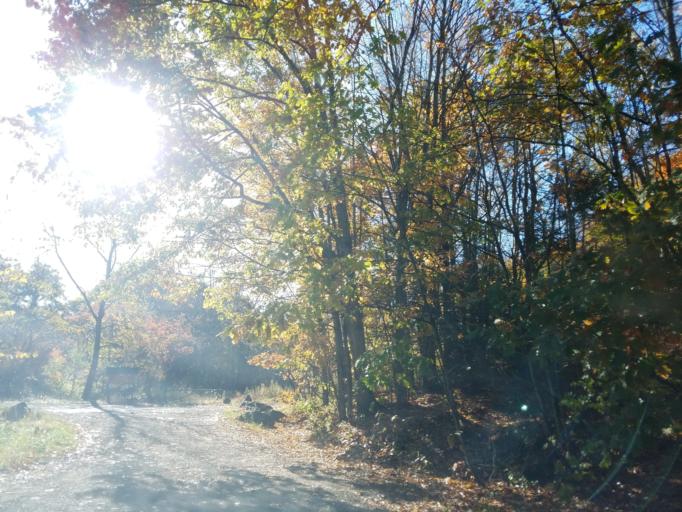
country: US
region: Connecticut
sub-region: Litchfield County
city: Winchester Center
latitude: 41.9426
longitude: -73.1120
